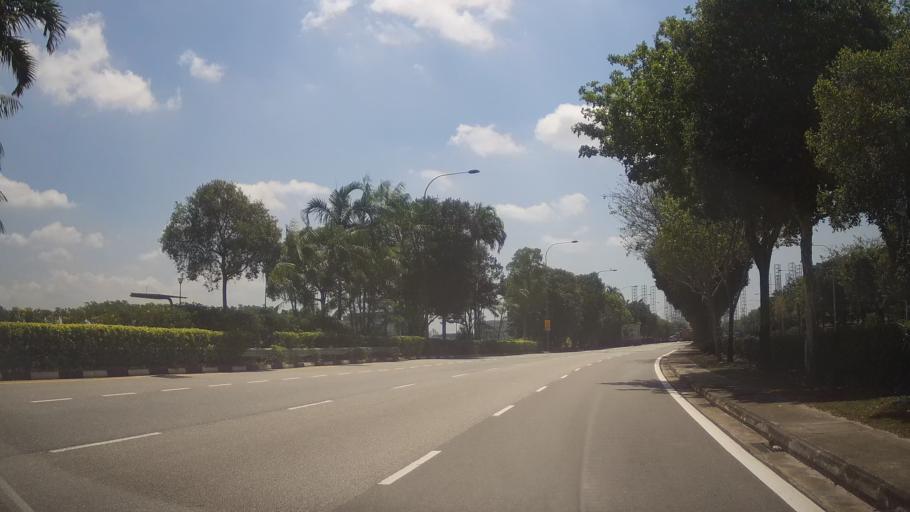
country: SG
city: Singapore
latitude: 1.3098
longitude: 103.7381
